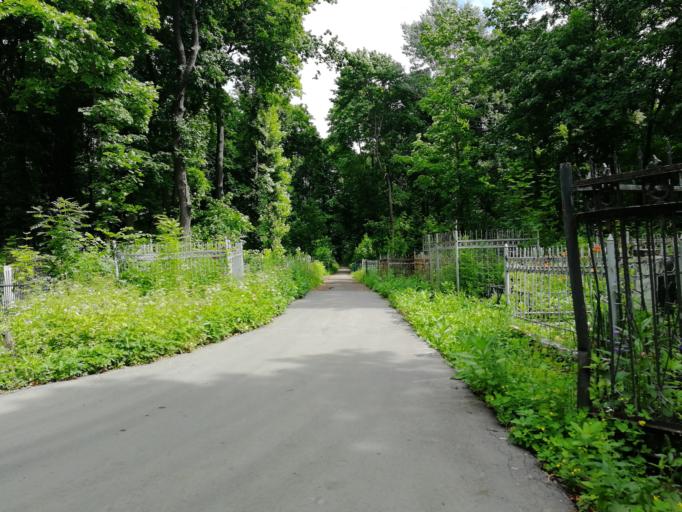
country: RU
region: Tula
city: Tula
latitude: 54.1776
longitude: 37.6114
